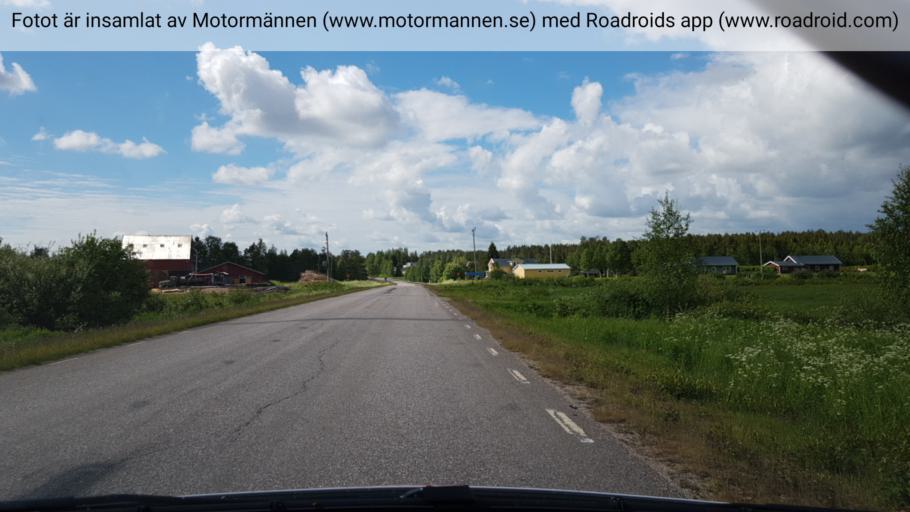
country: FI
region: Lapland
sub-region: Torniolaakso
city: Pello
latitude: 66.8052
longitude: 23.9026
